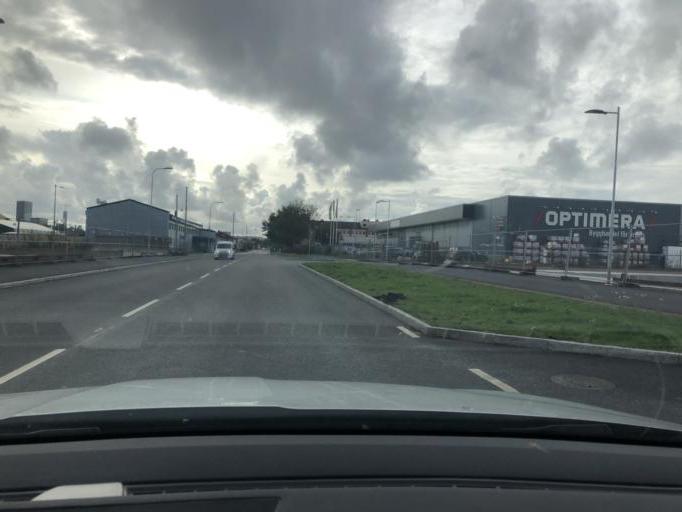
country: SE
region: Vaestra Goetaland
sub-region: Goteborg
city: Goeteborg
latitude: 57.7259
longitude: 11.9956
